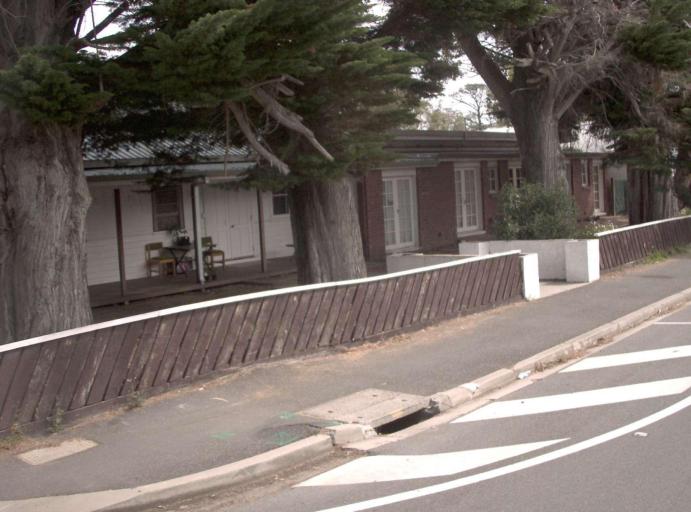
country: AU
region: Victoria
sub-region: Mornington Peninsula
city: Rosebud West
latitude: -38.3629
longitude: 144.8792
